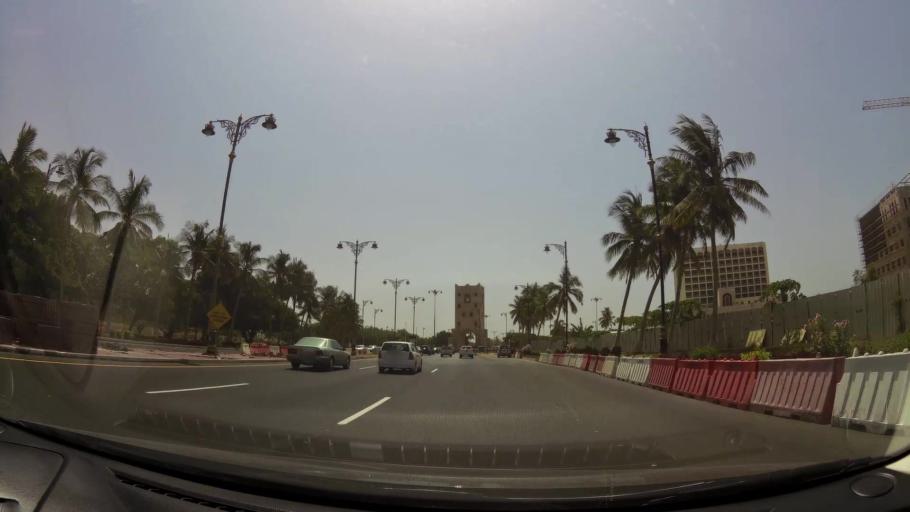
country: OM
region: Zufar
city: Salalah
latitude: 17.0249
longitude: 54.1097
